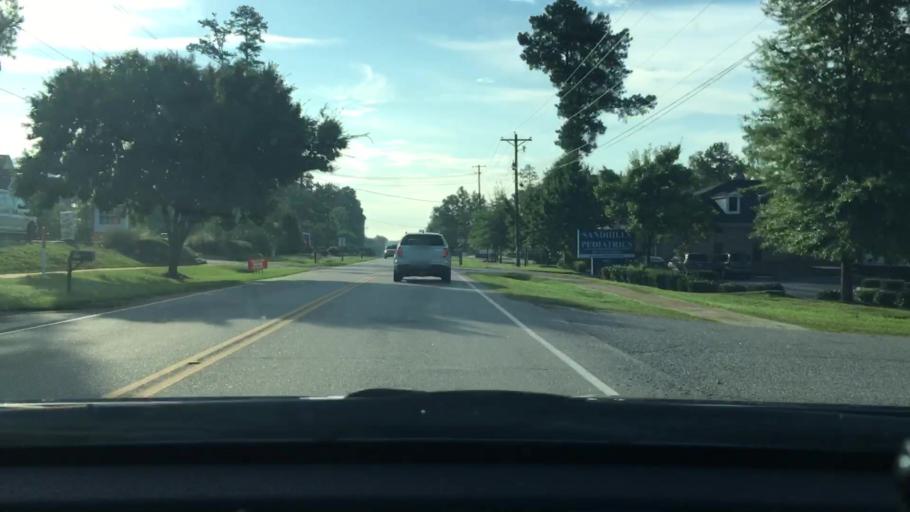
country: US
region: South Carolina
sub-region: Lexington County
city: Irmo
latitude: 34.1063
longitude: -81.1881
